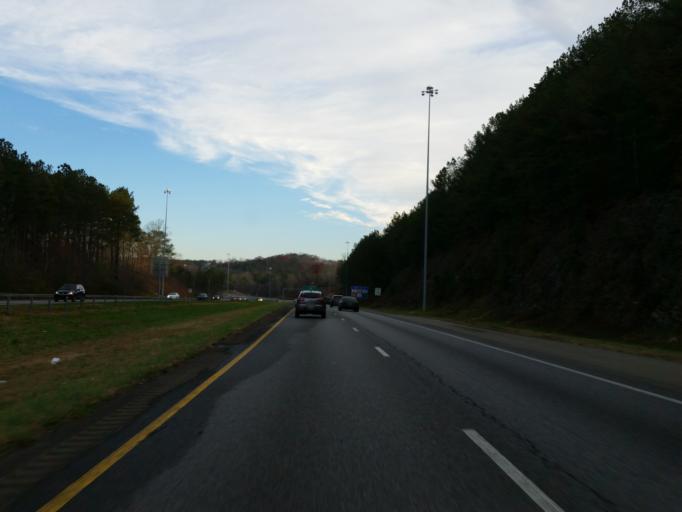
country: US
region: Georgia
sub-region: Cherokee County
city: Canton
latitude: 34.2270
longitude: -84.4730
